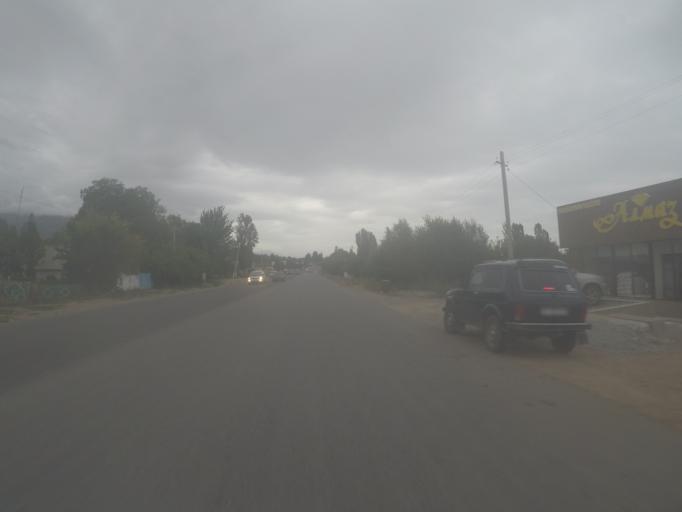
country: KG
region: Ysyk-Koel
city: Cholpon-Ata
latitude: 42.6891
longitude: 77.3505
